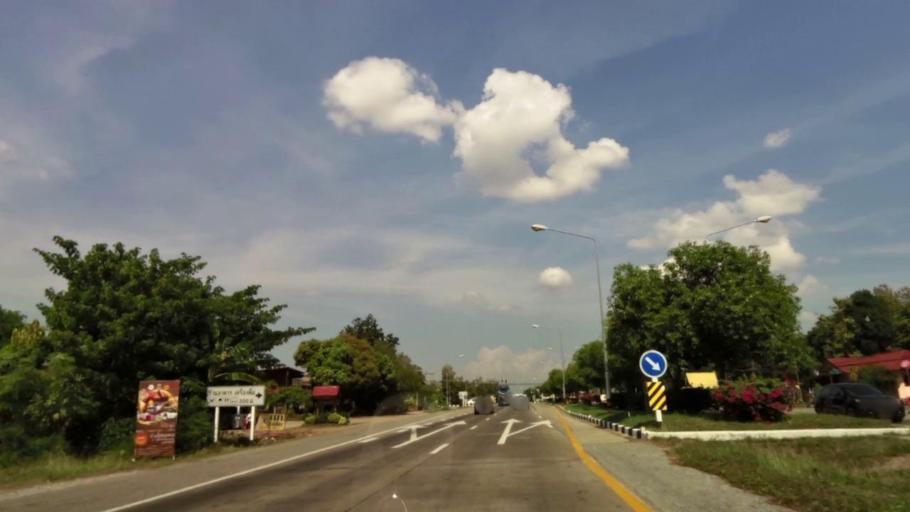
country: TH
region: Uttaradit
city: Thong Saen Khan
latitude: 17.4700
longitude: 100.2364
